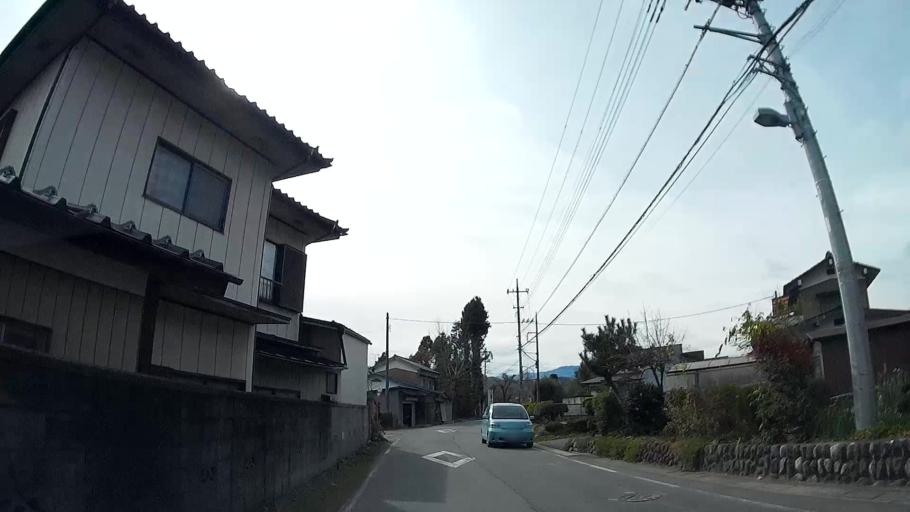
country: JP
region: Saitama
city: Chichibu
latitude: 36.0473
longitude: 139.0398
